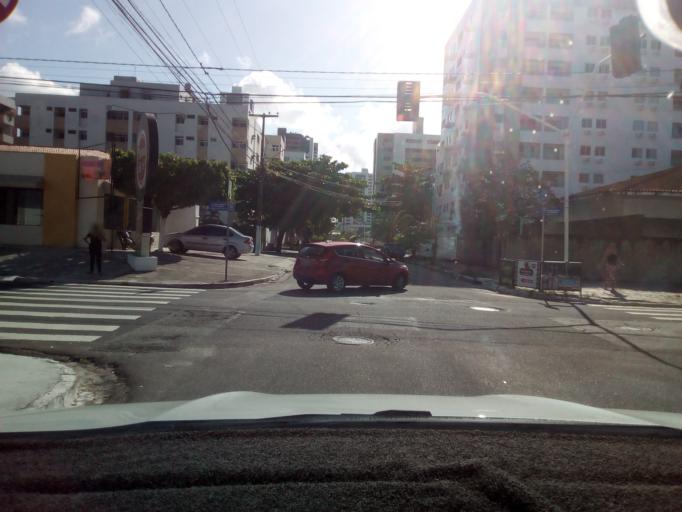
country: BR
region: Paraiba
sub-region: Joao Pessoa
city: Joao Pessoa
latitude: -7.1163
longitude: -34.8249
